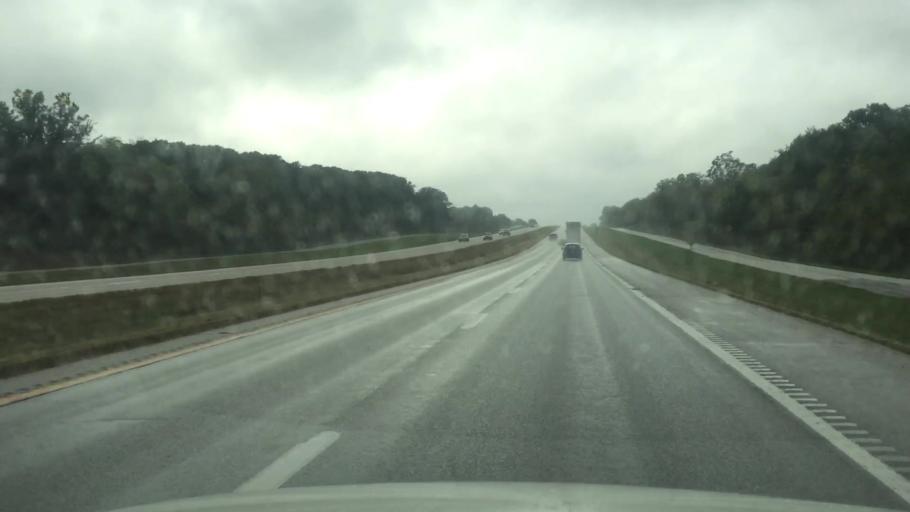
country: US
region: Missouri
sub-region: Cooper County
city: Boonville
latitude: 38.9349
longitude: -92.8762
